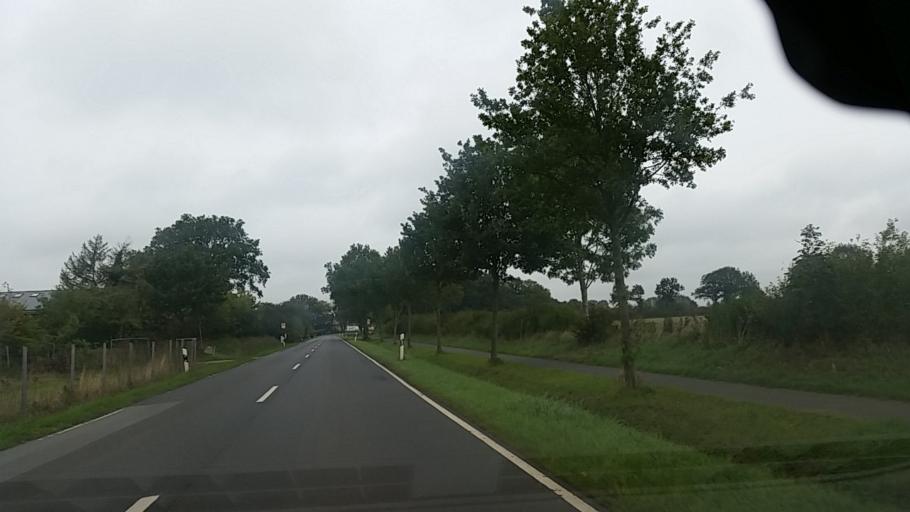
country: DE
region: Schleswig-Holstein
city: Schmalfeld
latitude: 53.8601
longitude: 9.9740
